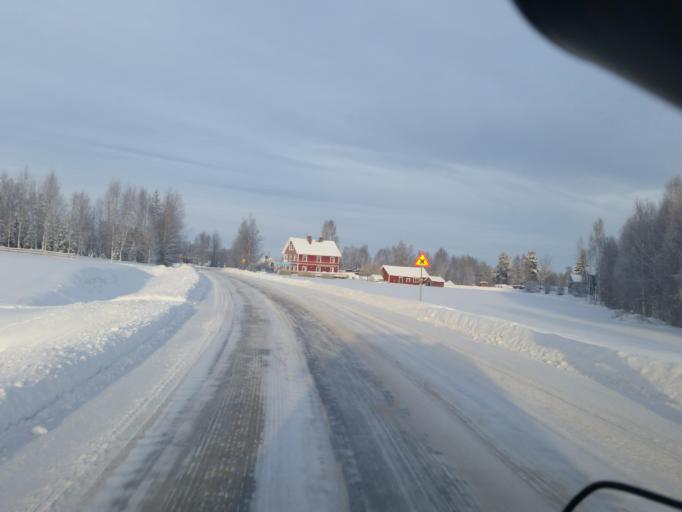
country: SE
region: Norrbotten
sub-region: Pitea Kommun
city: Norrfjarden
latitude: 65.5141
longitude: 21.4957
